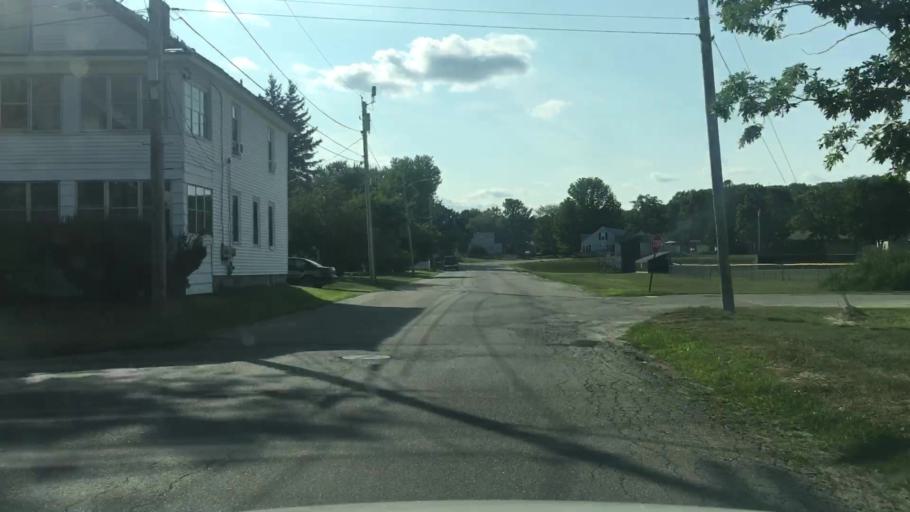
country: US
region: Maine
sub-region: Kennebec County
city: Waterville
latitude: 44.5510
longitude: -69.6436
